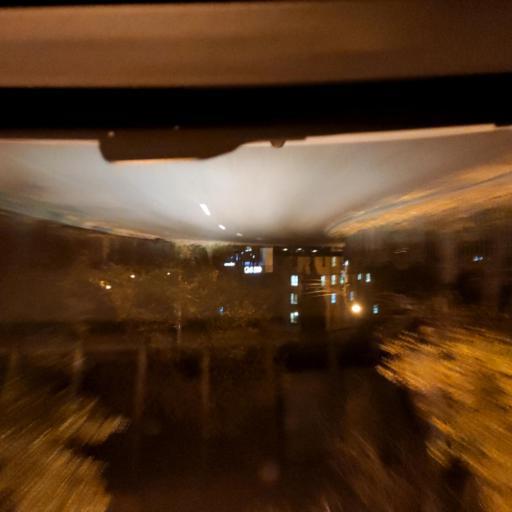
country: RU
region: Voronezj
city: Voronezh
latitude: 51.7103
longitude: 39.2300
